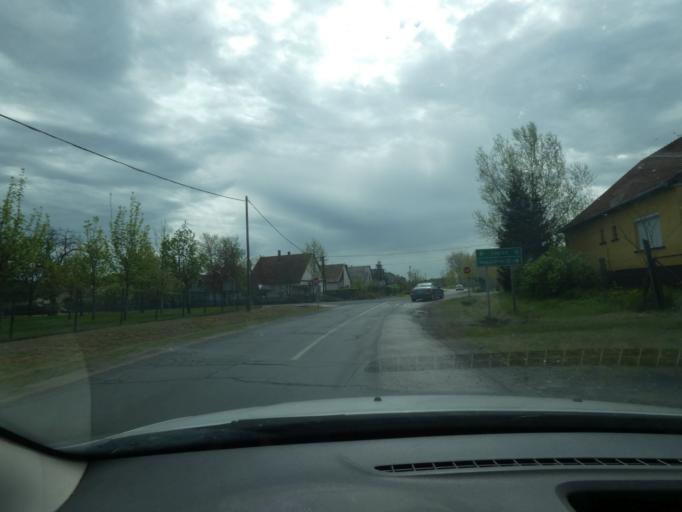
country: HU
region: Pest
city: Csemo
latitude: 47.1194
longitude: 19.6984
